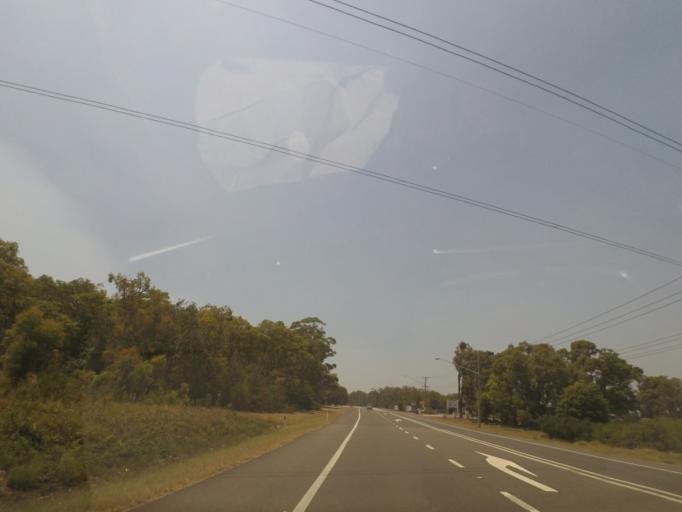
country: AU
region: New South Wales
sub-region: Newcastle
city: Beresfield
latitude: -32.8277
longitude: 151.7099
